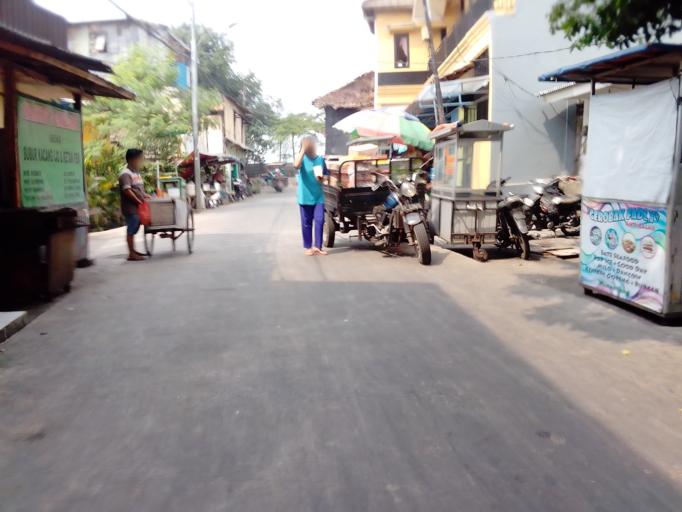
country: ID
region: Jakarta Raya
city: Jakarta
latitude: -6.1933
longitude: 106.8084
